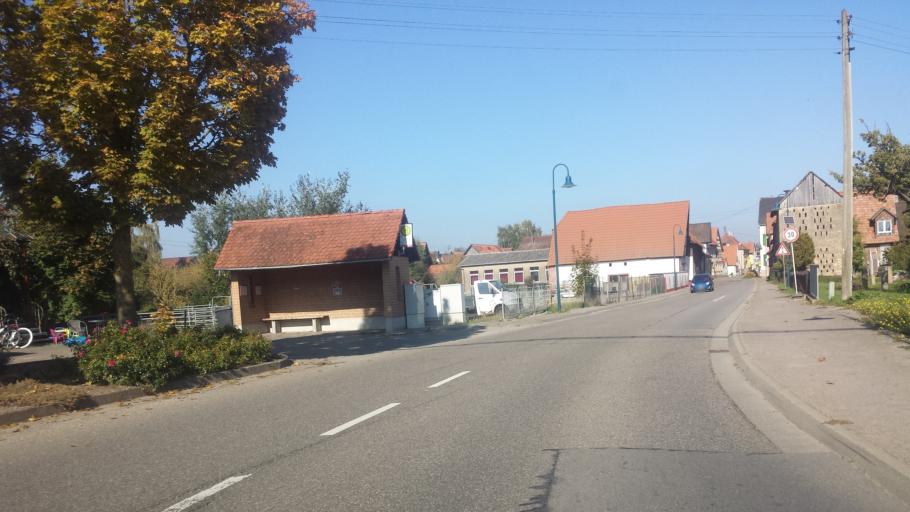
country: DE
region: Rheinland-Pfalz
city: Kandel
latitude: 49.1099
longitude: 8.1863
